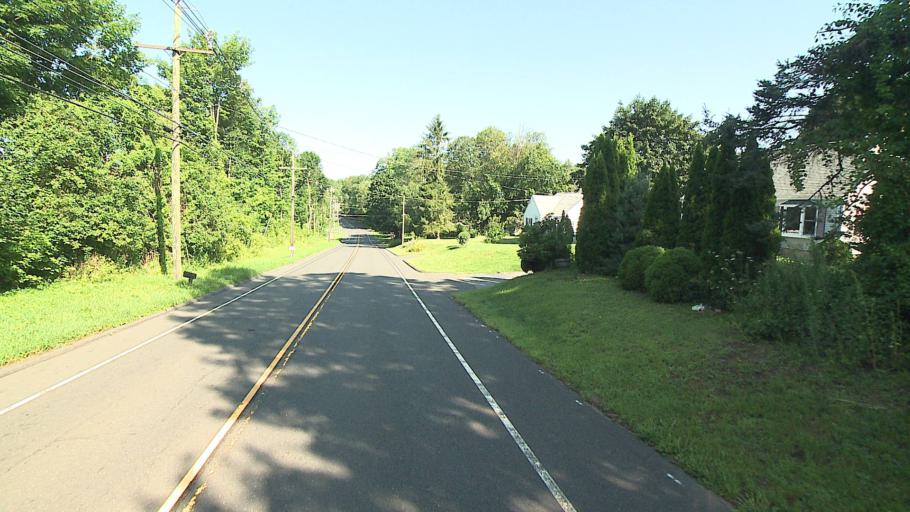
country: US
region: Connecticut
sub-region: Litchfield County
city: Litchfield
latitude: 41.8348
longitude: -73.2691
